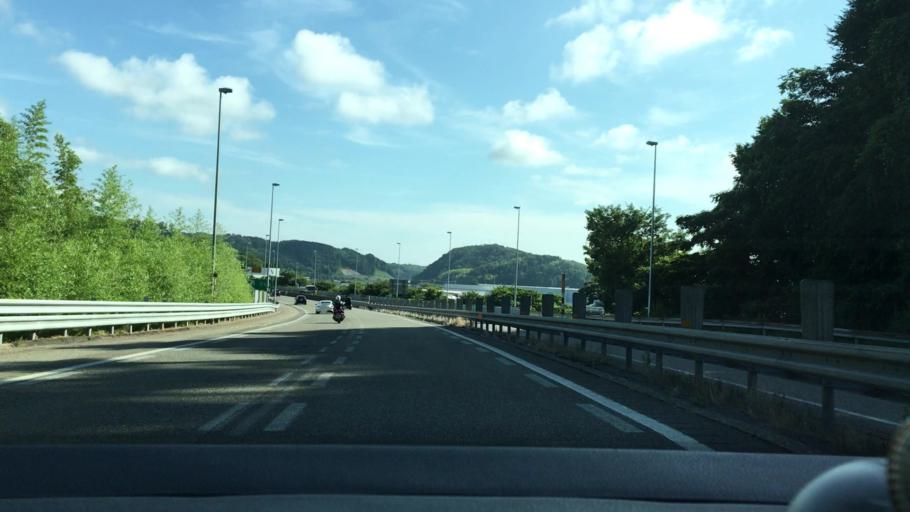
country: JP
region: Fukui
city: Maruoka
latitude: 36.3076
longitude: 136.2857
